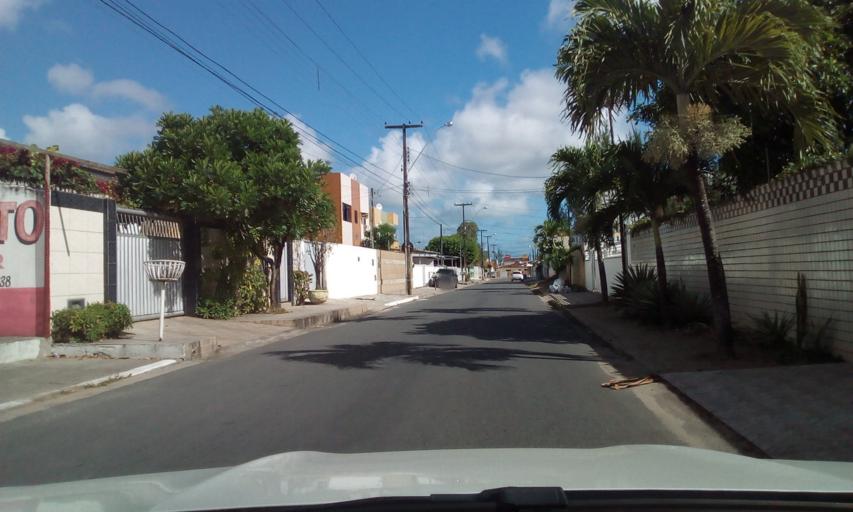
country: BR
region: Paraiba
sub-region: Joao Pessoa
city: Joao Pessoa
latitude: -7.1739
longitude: -34.8616
